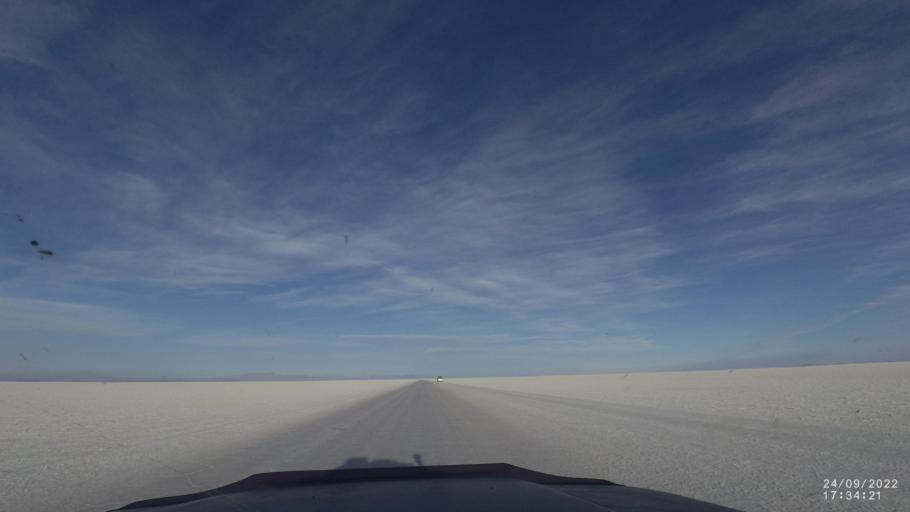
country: BO
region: Potosi
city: Colchani
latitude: -20.3207
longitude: -67.2840
